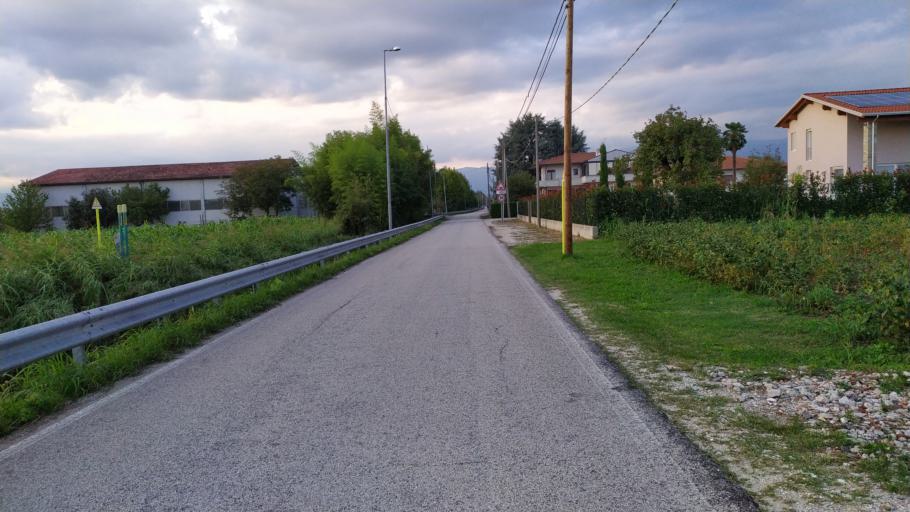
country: IT
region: Veneto
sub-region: Provincia di Vicenza
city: Novoledo
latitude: 45.6391
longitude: 11.5077
